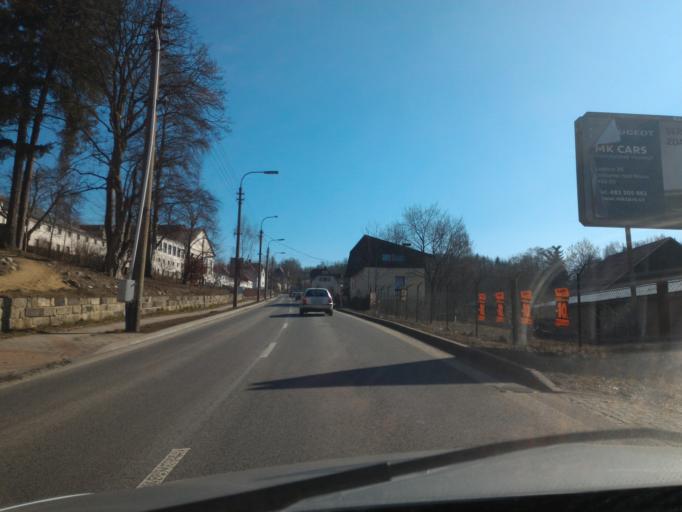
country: CZ
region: Liberecky
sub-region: Okres Jablonec nad Nisou
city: Lucany nad Nisou
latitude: 50.7408
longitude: 15.2256
